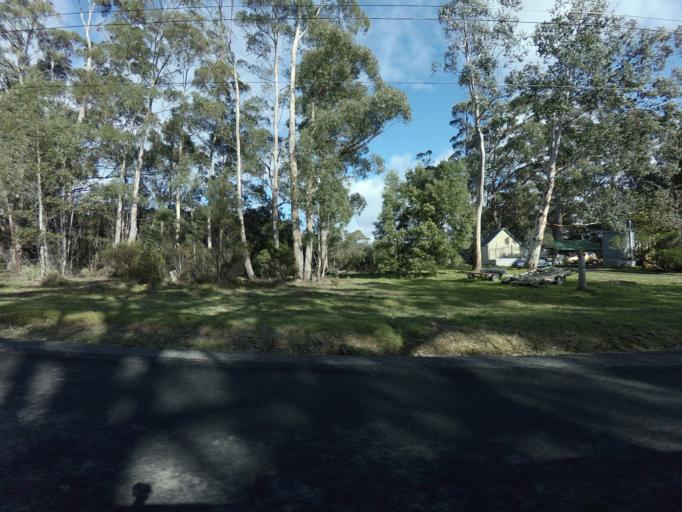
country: AU
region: Tasmania
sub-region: Huon Valley
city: Geeveston
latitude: -43.4327
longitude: 146.9034
